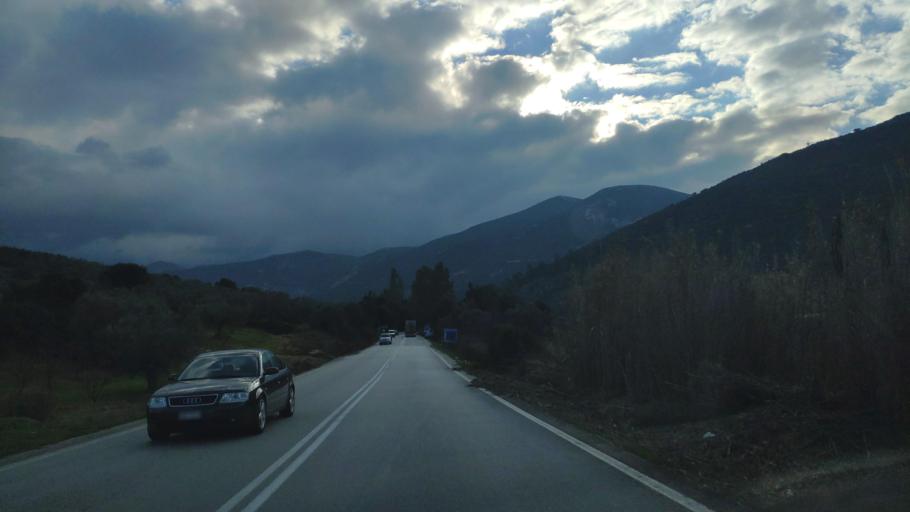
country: GR
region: Peloponnese
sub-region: Nomos Korinthias
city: Ayios Vasilios
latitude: 37.7917
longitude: 22.7426
